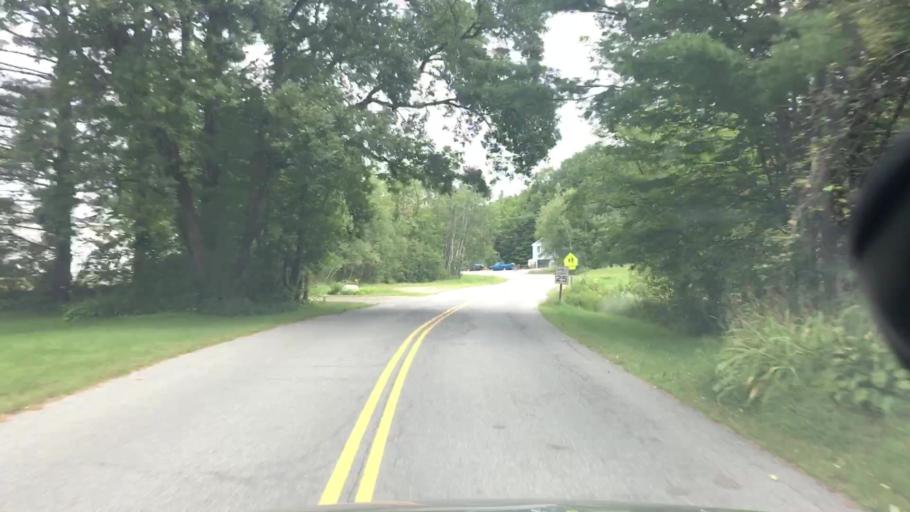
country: US
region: Massachusetts
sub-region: Franklin County
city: Colrain
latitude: 42.7829
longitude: -72.7685
